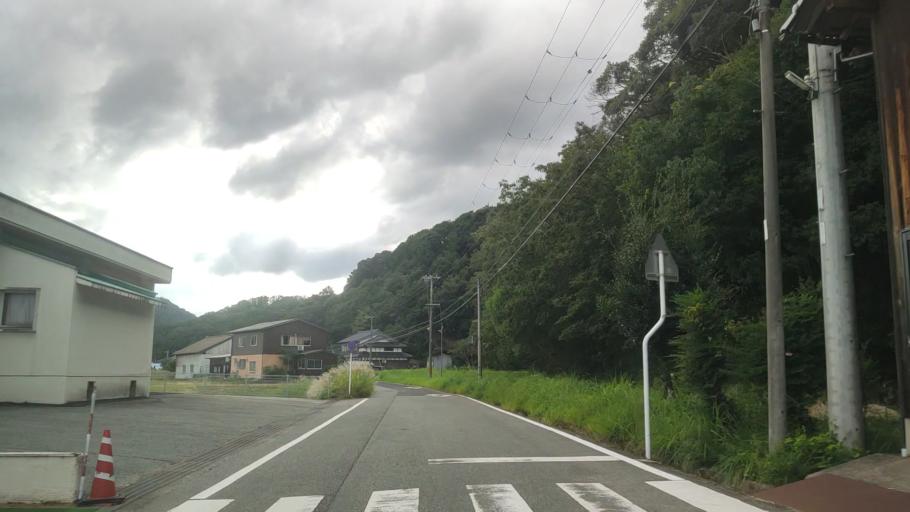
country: JP
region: Hyogo
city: Toyooka
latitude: 35.6035
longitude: 134.8918
